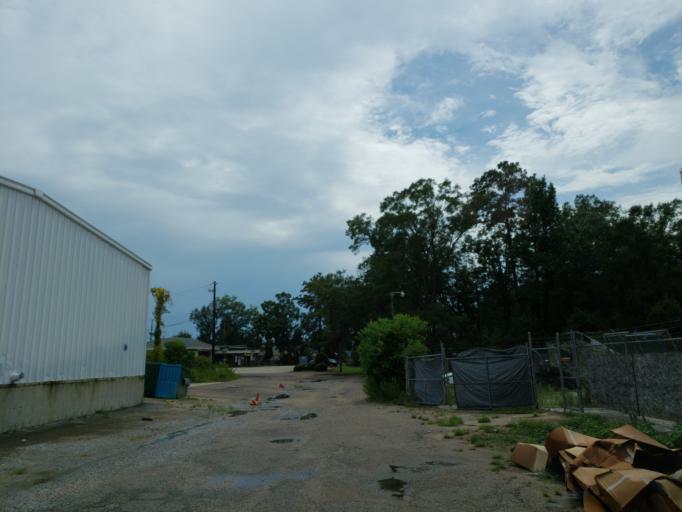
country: US
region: Mississippi
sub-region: Forrest County
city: Hattiesburg
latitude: 31.3130
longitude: -89.3111
